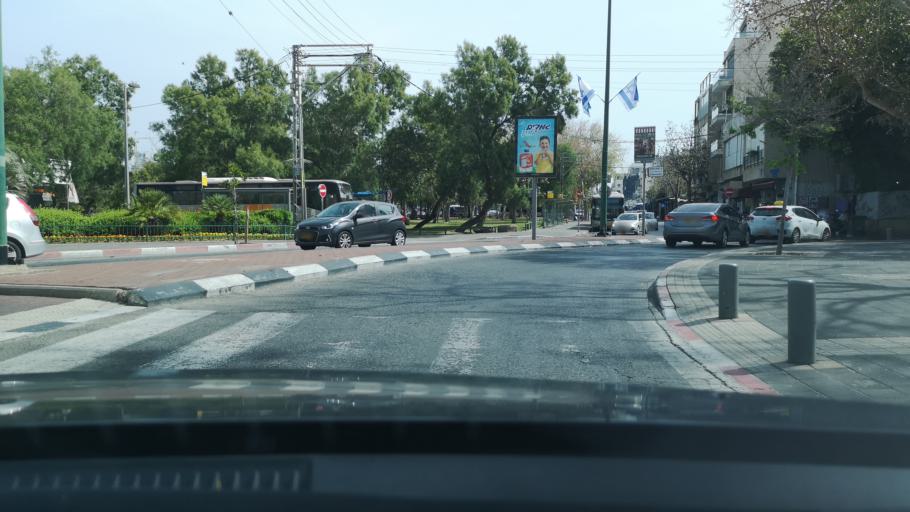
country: IL
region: Tel Aviv
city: Yafo
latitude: 32.0655
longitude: 34.7650
